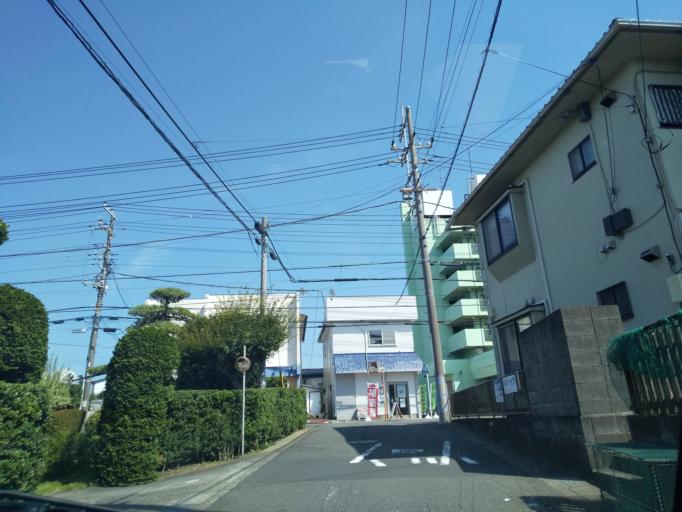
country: JP
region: Kanagawa
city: Minami-rinkan
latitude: 35.4657
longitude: 139.4179
